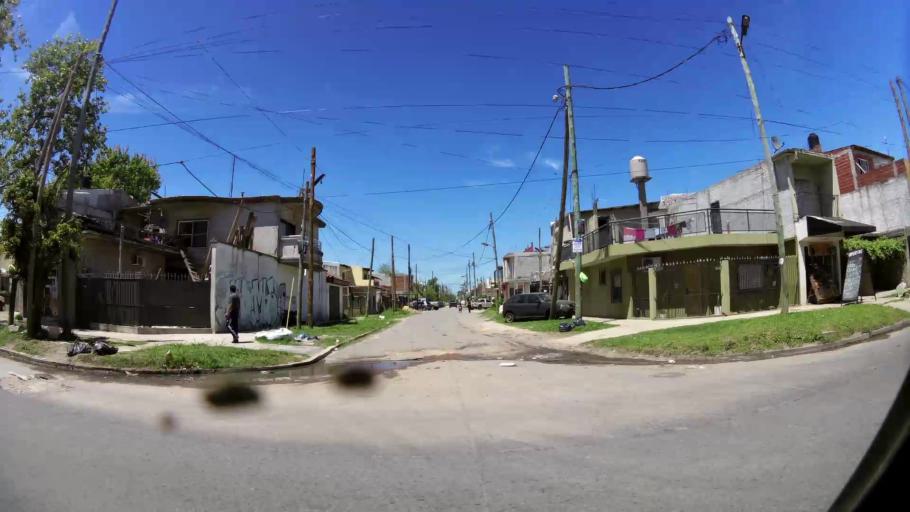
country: AR
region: Buenos Aires
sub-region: Partido de Quilmes
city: Quilmes
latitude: -34.7139
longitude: -58.3198
